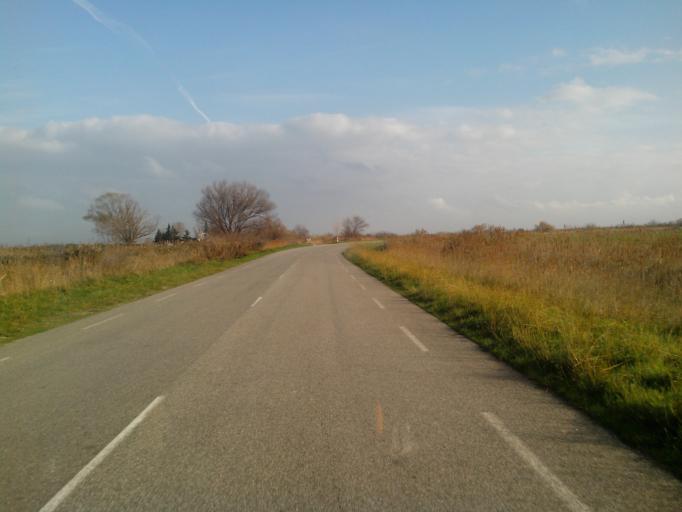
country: FR
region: Languedoc-Roussillon
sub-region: Departement du Gard
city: Saint-Gilles
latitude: 43.6054
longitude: 4.4853
